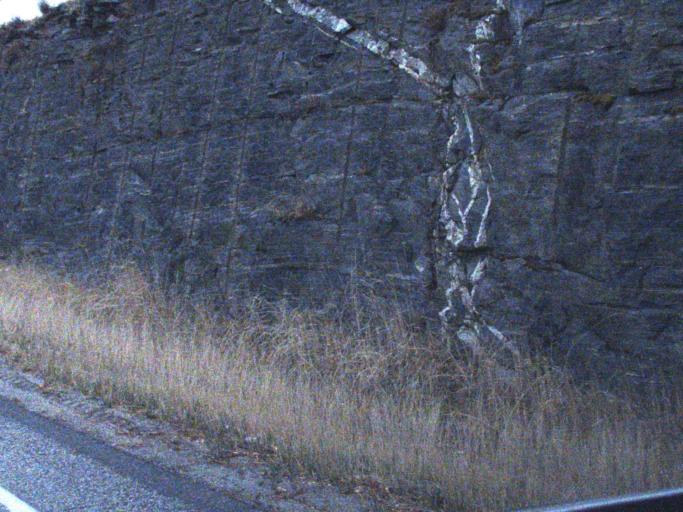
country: US
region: Washington
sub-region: Stevens County
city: Kettle Falls
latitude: 48.6489
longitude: -118.1127
